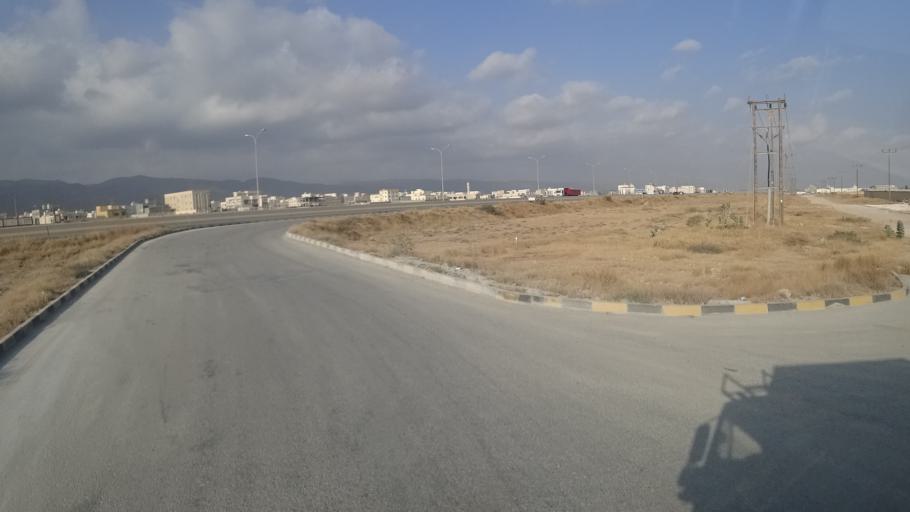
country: OM
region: Zufar
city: Salalah
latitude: 17.0352
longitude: 54.0380
